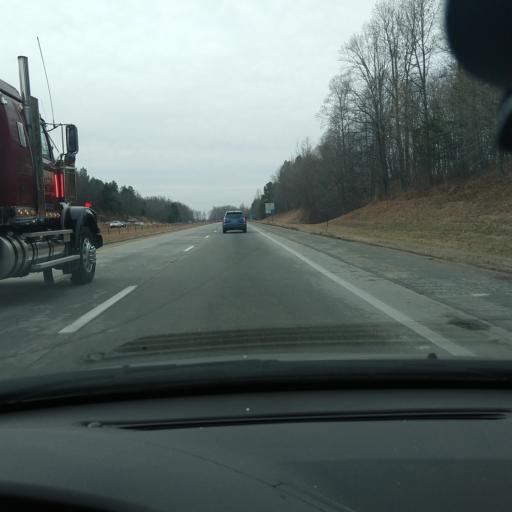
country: US
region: North Carolina
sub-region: Davidson County
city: Lexington
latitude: 35.8510
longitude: -80.2761
